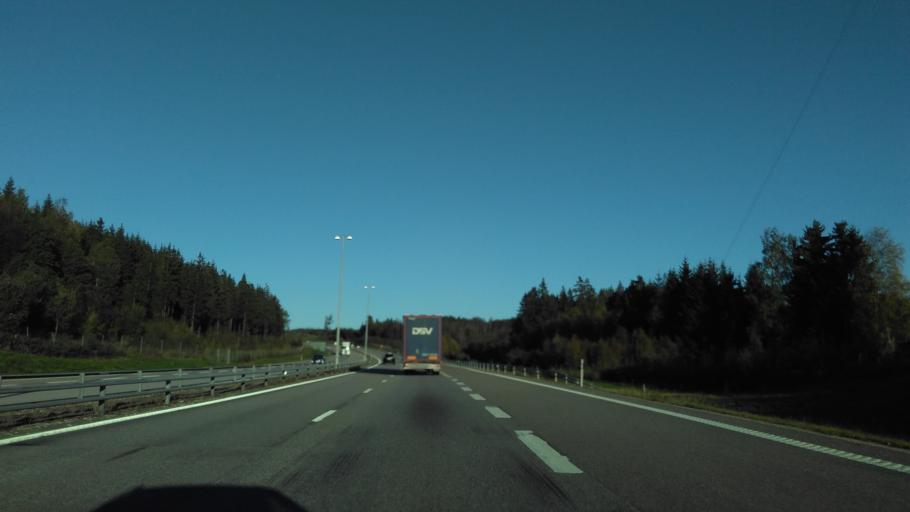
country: SE
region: Vaestra Goetaland
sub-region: Boras Kommun
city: Ganghester
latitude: 57.7281
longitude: 13.0176
